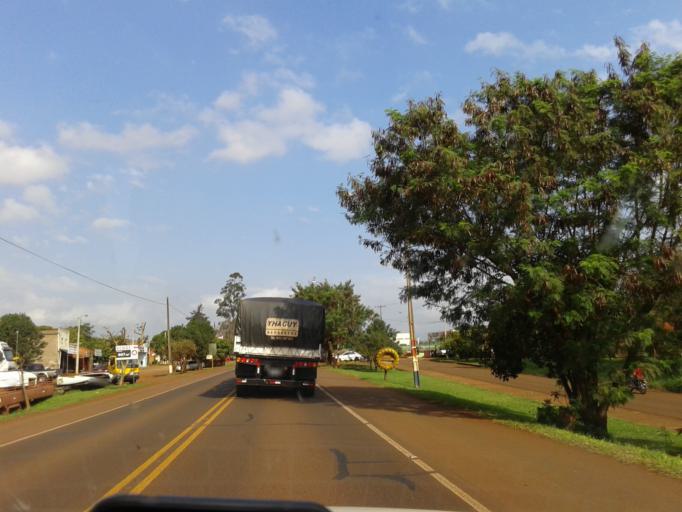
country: PY
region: Itapua
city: Arquitecto Tomas Romero Pereira
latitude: -26.4973
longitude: -55.2786
